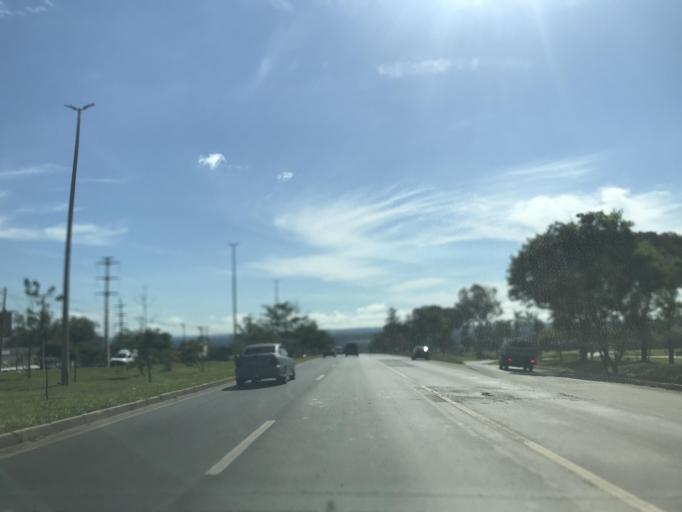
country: BR
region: Federal District
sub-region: Brasilia
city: Brasilia
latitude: -15.8782
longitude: -47.9963
